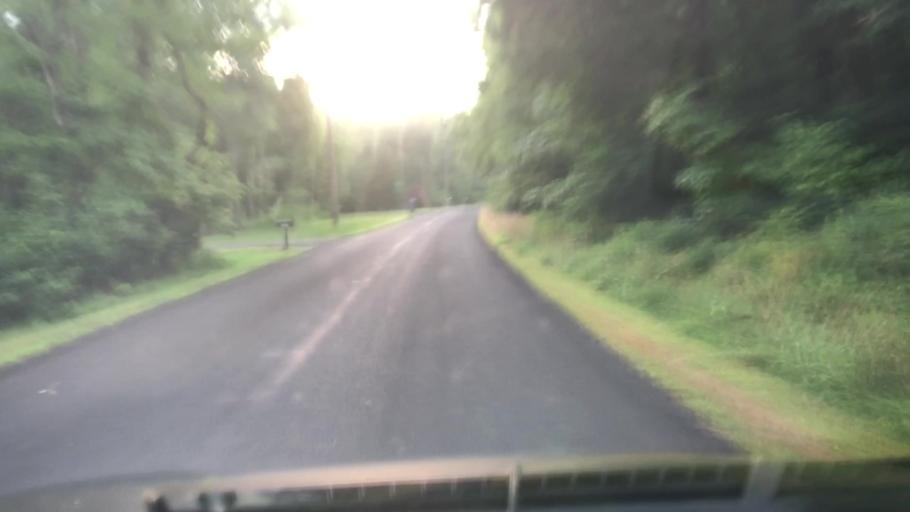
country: US
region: Virginia
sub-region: Fauquier County
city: New Baltimore
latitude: 38.7132
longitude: -77.6702
